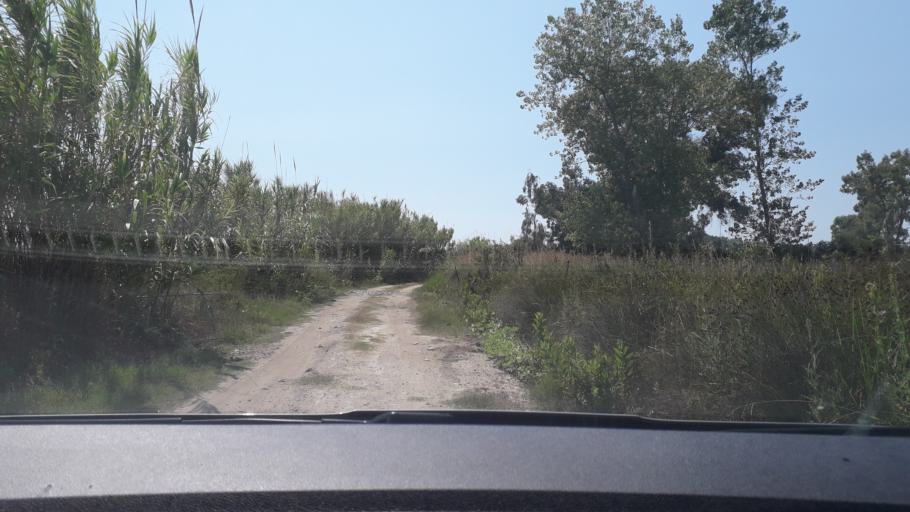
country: GR
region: Ionian Islands
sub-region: Nomos Kerkyras
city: Agios Matthaios
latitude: 39.4552
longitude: 19.8840
